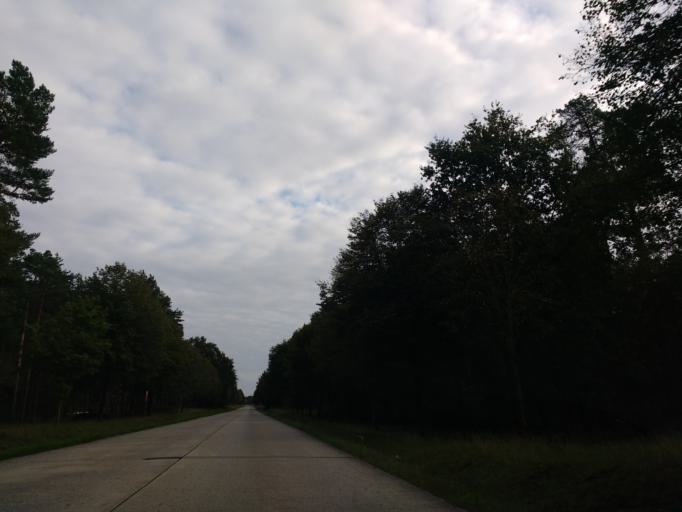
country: DE
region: North Rhine-Westphalia
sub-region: Regierungsbezirk Detmold
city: Hovelhof
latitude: 51.8411
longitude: 8.6984
